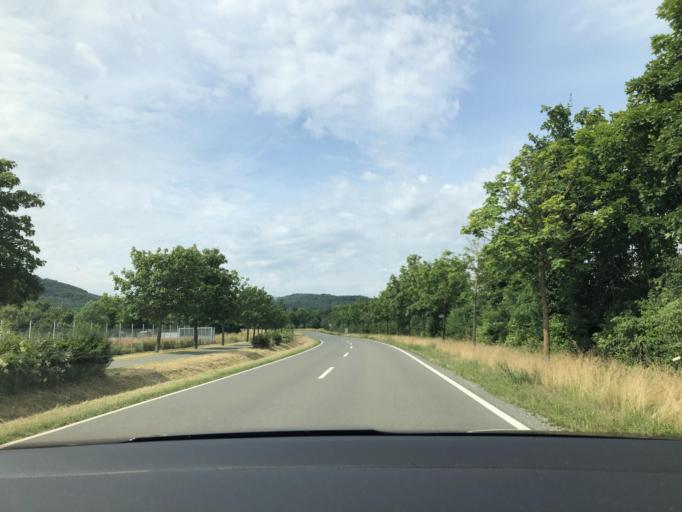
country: DE
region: Saxony-Anhalt
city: Blankenburg
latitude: 51.8112
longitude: 10.9316
